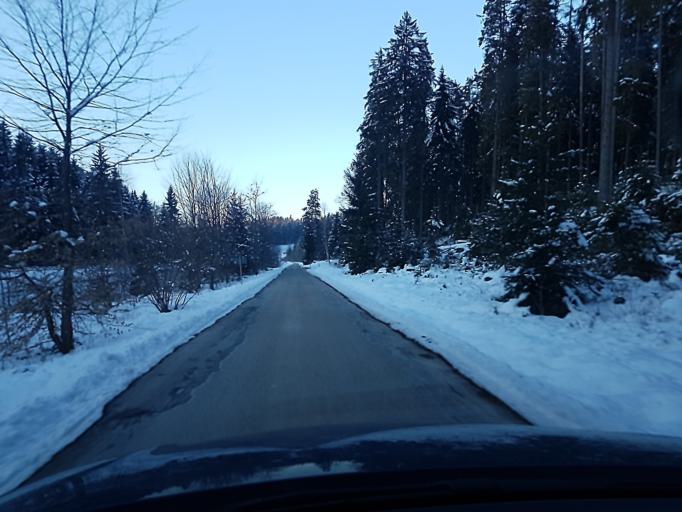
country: DE
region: Baden-Wuerttemberg
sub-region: Freiburg Region
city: Monchweiler
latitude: 48.0846
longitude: 8.4050
